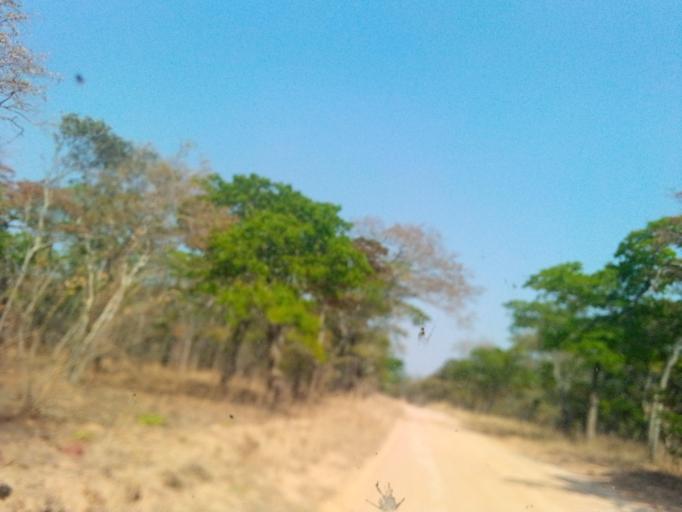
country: ZM
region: Northern
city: Mpika
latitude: -12.2419
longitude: 30.8606
